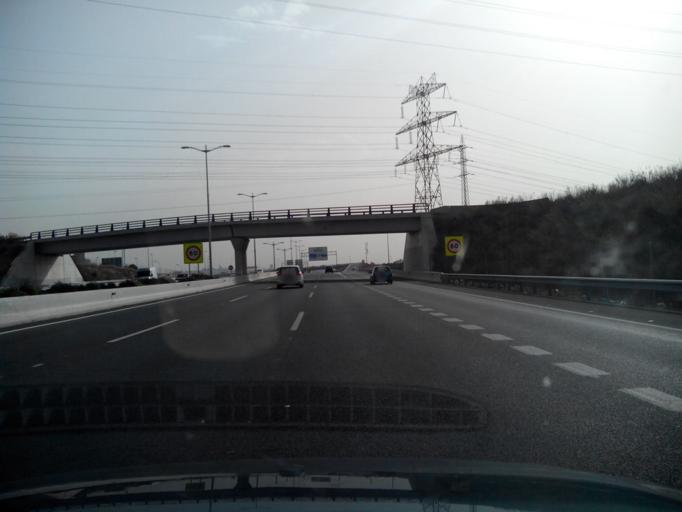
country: ES
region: Catalonia
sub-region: Provincia de Tarragona
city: Constanti
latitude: 41.1299
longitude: 1.1952
